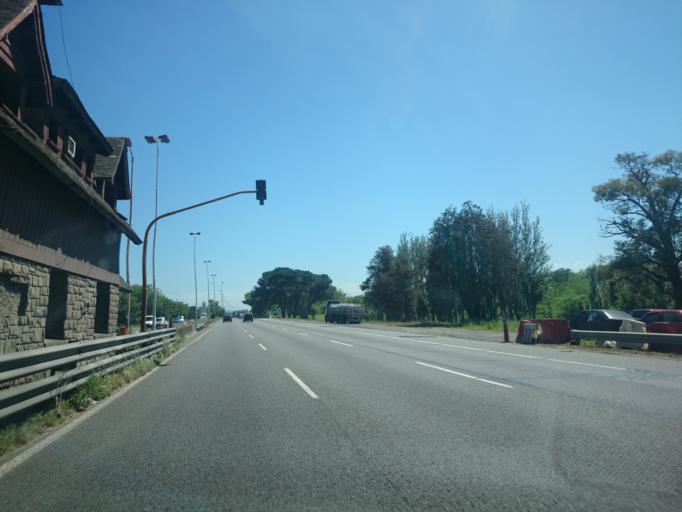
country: AR
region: Buenos Aires
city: San Justo
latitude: -34.7499
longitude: -58.5225
